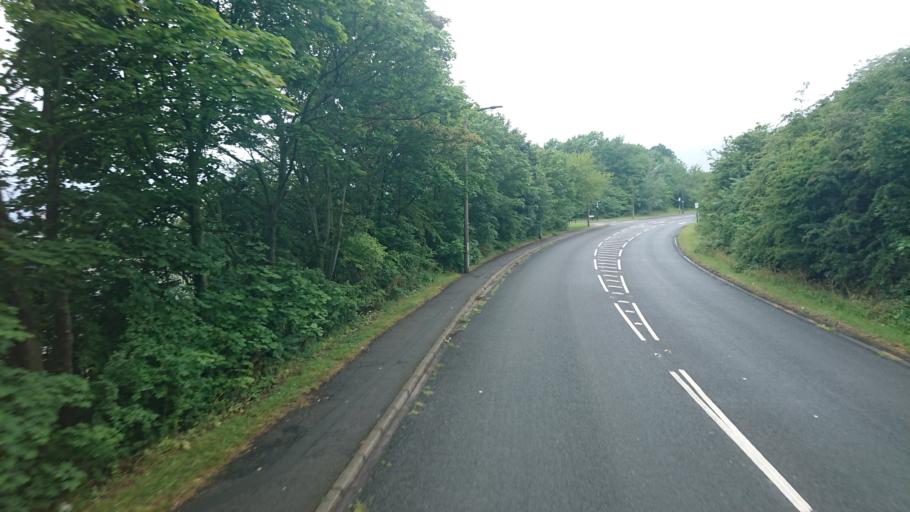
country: GB
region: England
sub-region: Rotherham
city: Catcliffe
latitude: 53.3977
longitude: -1.3756
